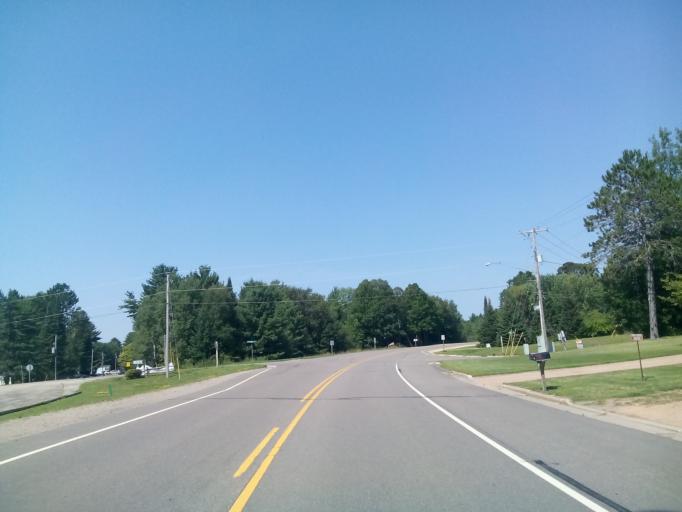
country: US
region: Wisconsin
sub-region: Menominee County
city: Legend Lake
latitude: 45.3014
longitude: -88.5419
